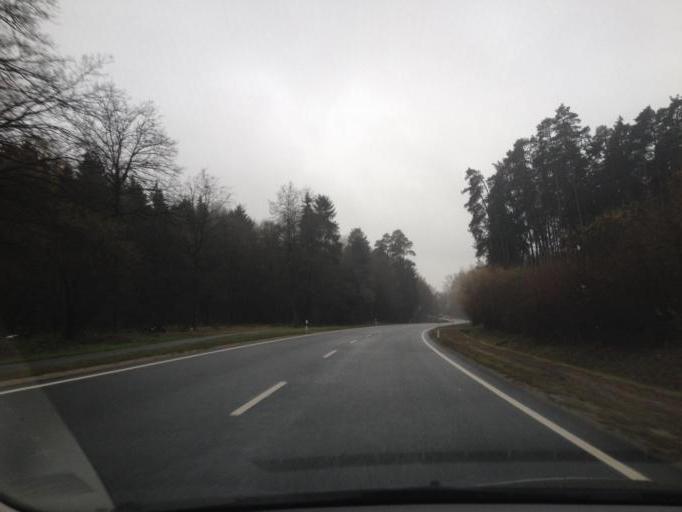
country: DE
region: Bavaria
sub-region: Regierungsbezirk Mittelfranken
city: Heroldsberg
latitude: 49.5520
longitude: 11.1670
